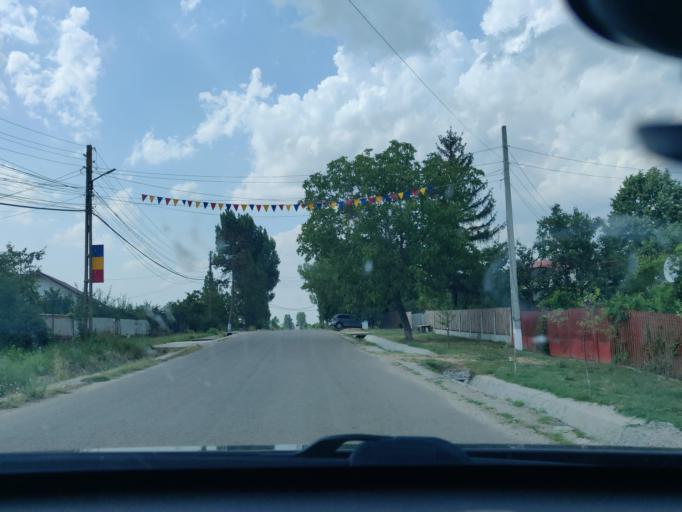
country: RO
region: Teleorman
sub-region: Comuna Sarbeni
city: Sarbeni
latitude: 44.4588
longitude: 25.4001
